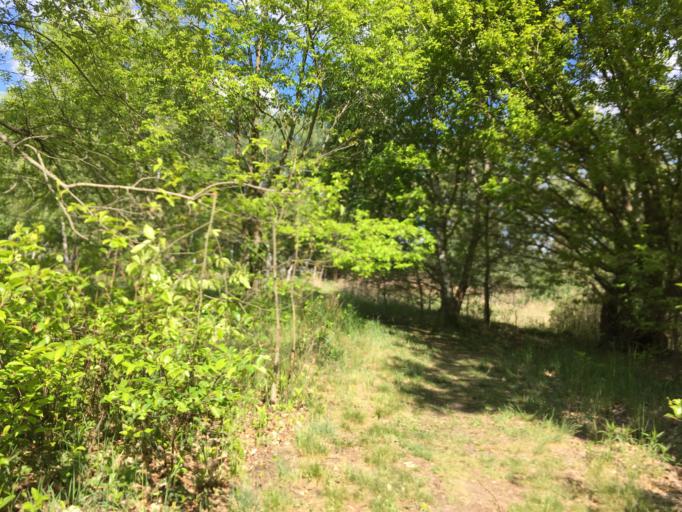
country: DE
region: Berlin
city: Blankenfelde
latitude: 52.6545
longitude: 13.3812
